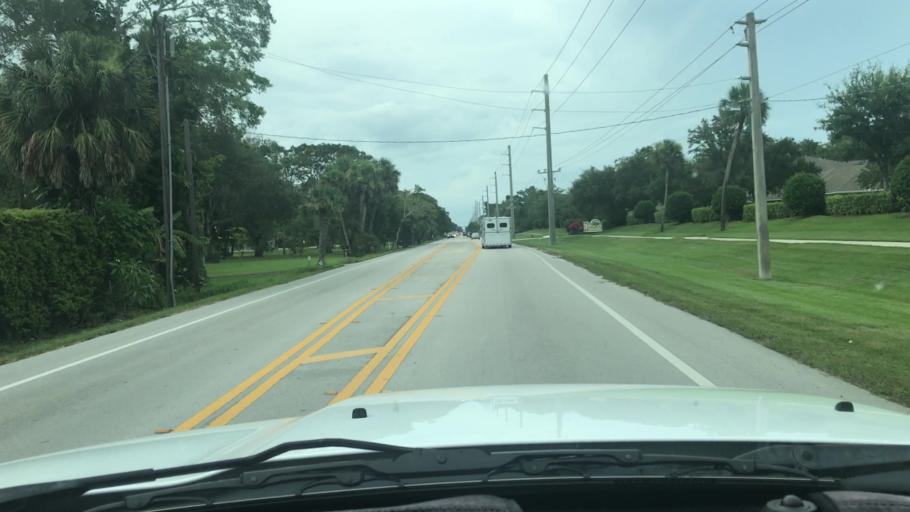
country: US
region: Florida
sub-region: Indian River County
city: Florida Ridge
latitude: 27.5810
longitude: -80.4142
